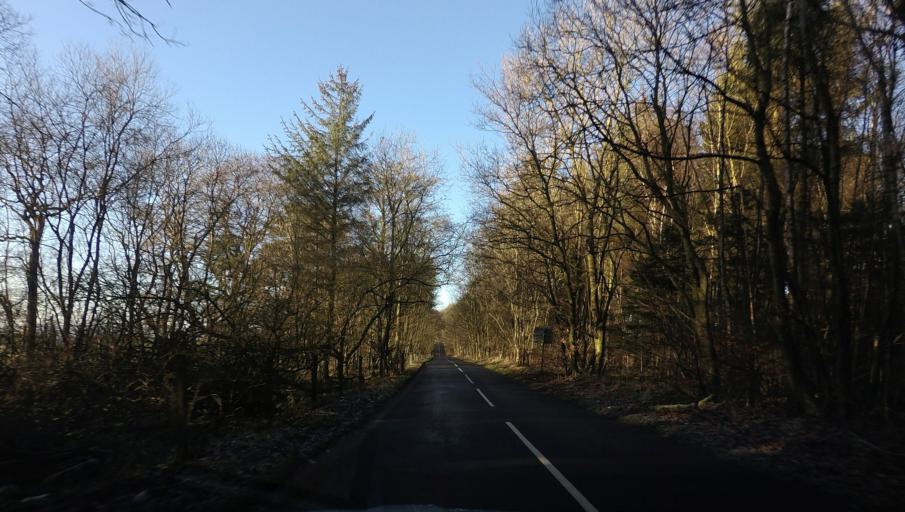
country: GB
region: Scotland
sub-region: North Lanarkshire
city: Newmains
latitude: 55.8050
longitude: -3.8722
